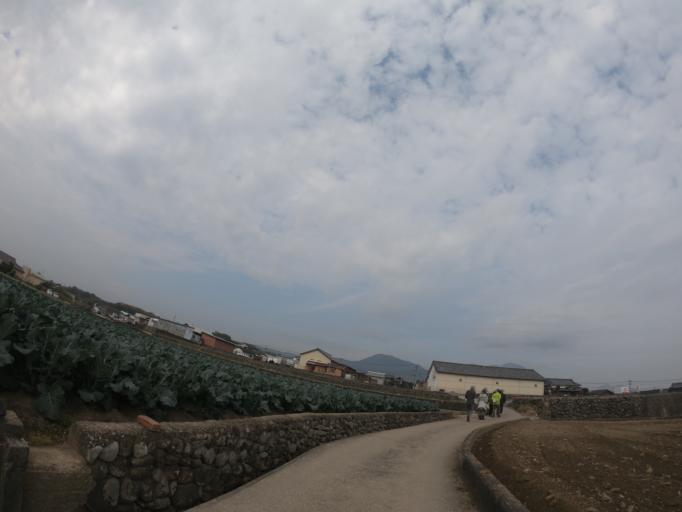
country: JP
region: Nagasaki
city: Shimabara
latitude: 32.6598
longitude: 130.3031
